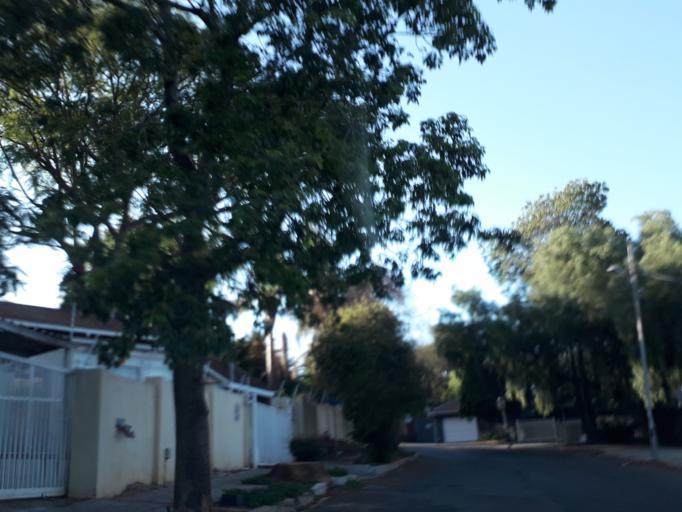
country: ZA
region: Gauteng
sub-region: City of Johannesburg Metropolitan Municipality
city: Johannesburg
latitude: -26.1733
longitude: 27.9928
